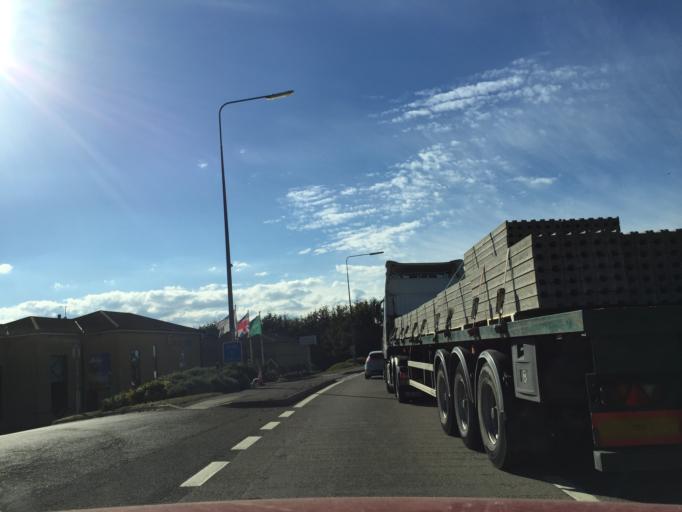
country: GB
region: England
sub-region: Warwickshire
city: Ryton on Dunsmore
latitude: 52.3741
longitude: -1.4589
